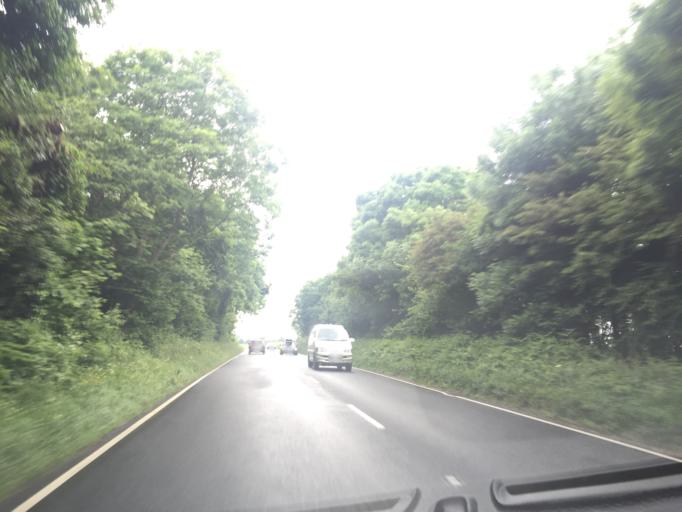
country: GB
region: England
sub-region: Dorset
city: Bovington Camp
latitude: 50.6630
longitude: -2.3062
